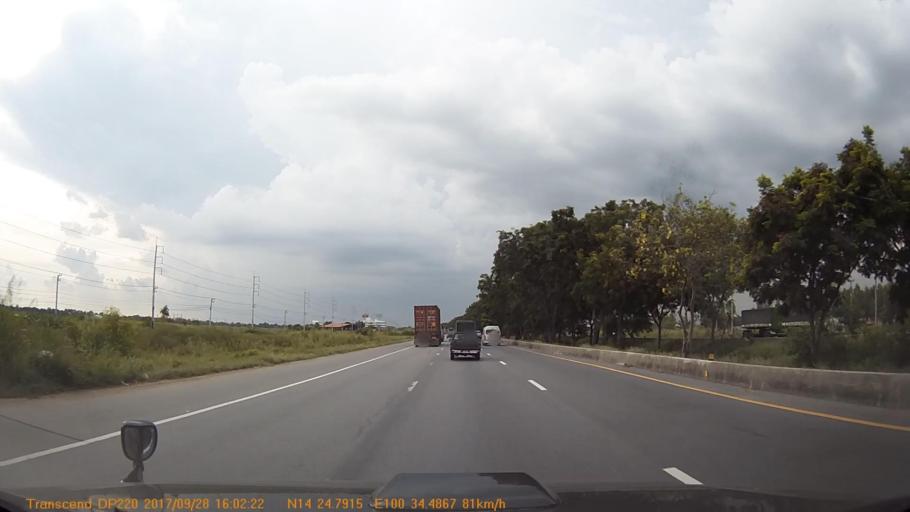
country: TH
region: Phra Nakhon Si Ayutthaya
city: Bang Pahan
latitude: 14.4132
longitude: 100.5748
